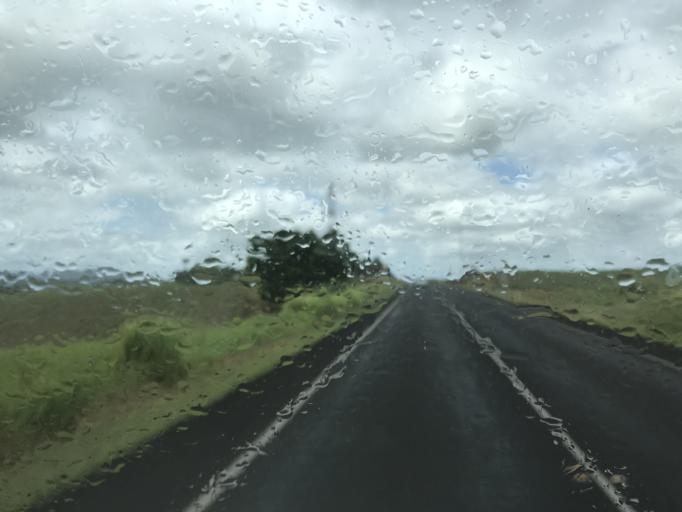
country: AU
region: Queensland
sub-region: Cassowary Coast
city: Innisfail
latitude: -17.5792
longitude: 145.9879
